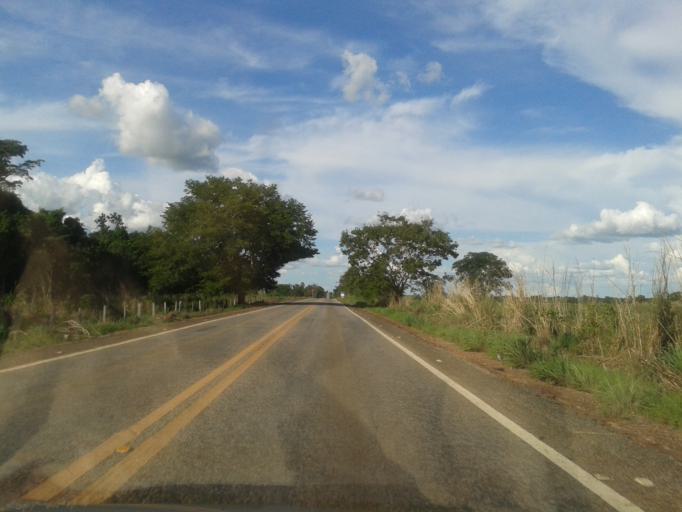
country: BR
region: Goias
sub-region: Mozarlandia
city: Mozarlandia
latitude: -14.5539
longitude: -50.4946
